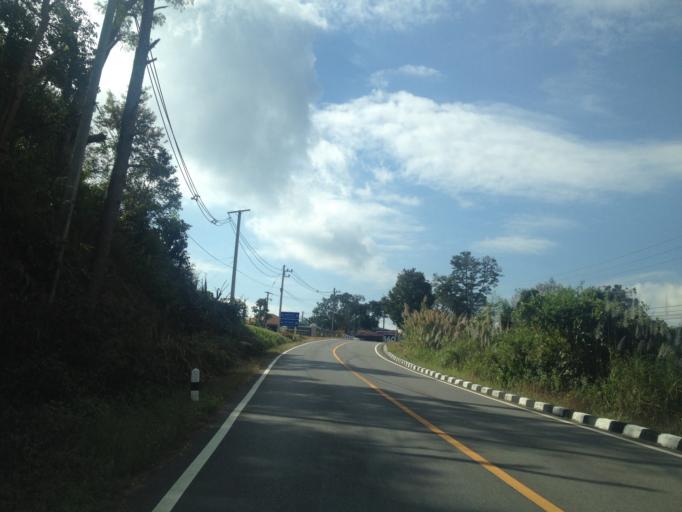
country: TH
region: Mae Hong Son
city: Ban Huai I Huak
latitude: 18.1488
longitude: 98.1593
